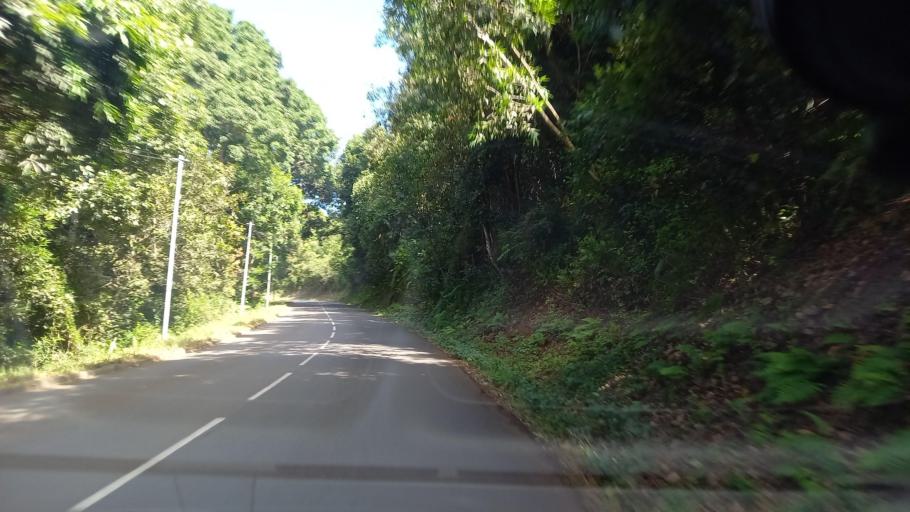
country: YT
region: Dembeni
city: Dembeni
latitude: -12.7873
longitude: 45.1651
